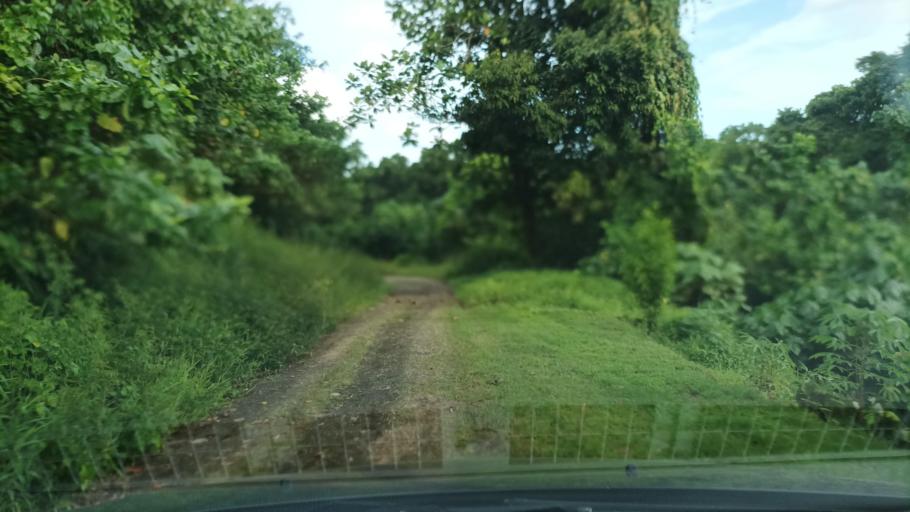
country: FM
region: Kosrae
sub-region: Utwe Municipality
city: Utwe
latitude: 5.2753
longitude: 162.9517
